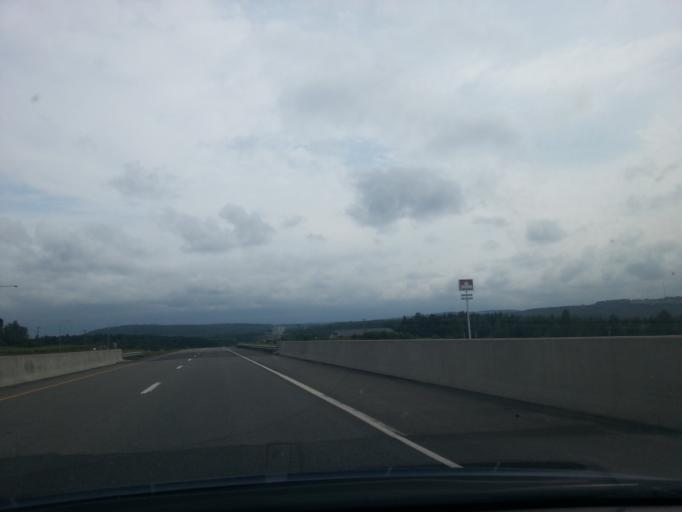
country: US
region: Maine
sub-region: Aroostook County
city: Houlton
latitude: 46.1741
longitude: -67.6086
